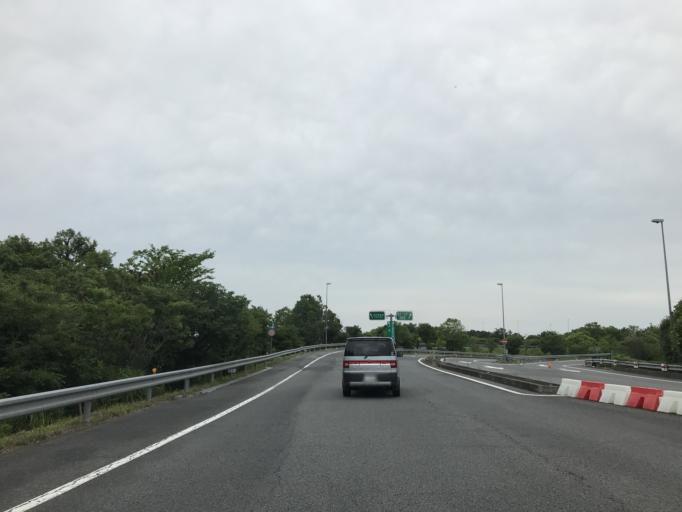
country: JP
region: Ibaraki
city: Mito-shi
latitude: 36.3164
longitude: 140.4559
